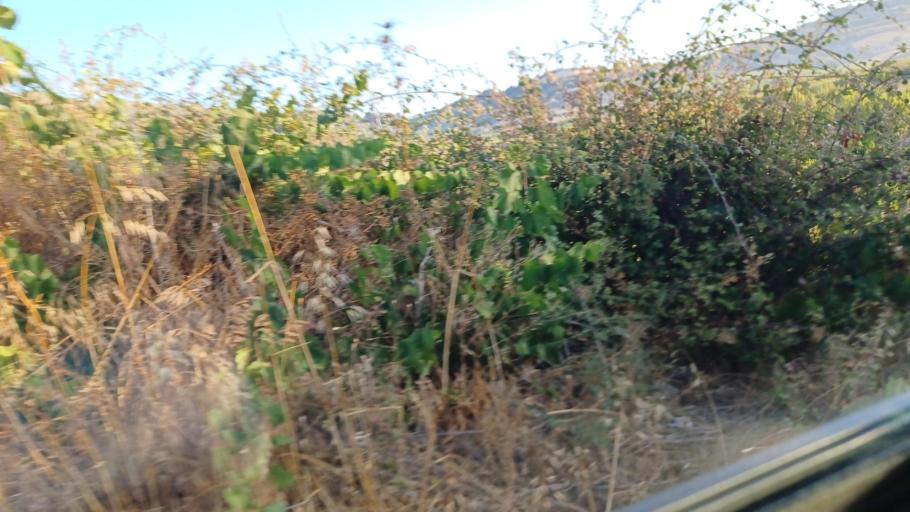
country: CY
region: Pafos
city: Mesogi
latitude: 34.8678
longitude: 32.4911
